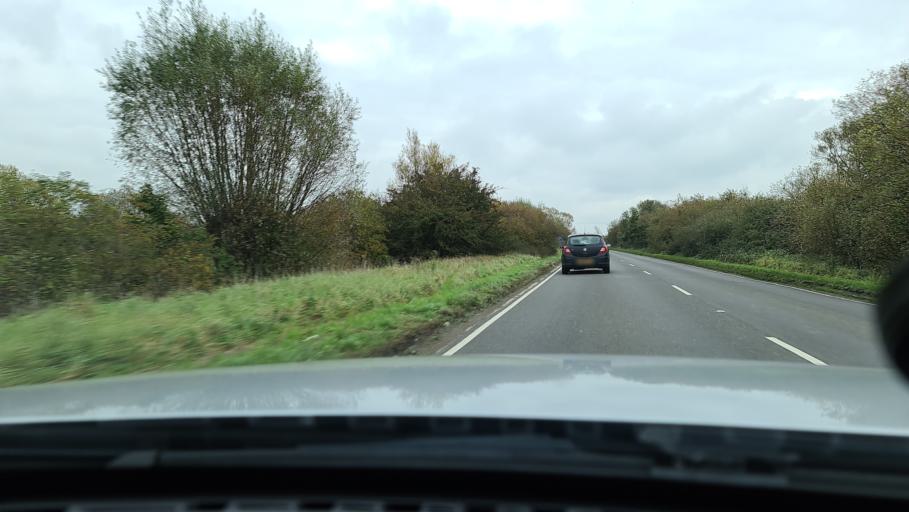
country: GB
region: England
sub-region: Oxfordshire
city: Bicester
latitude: 51.8744
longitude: -1.0721
